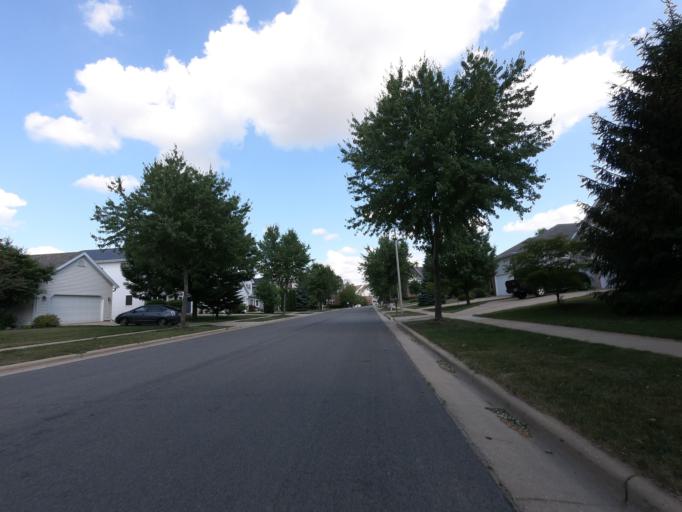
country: US
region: Wisconsin
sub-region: Dane County
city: Middleton
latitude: 43.0760
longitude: -89.5538
